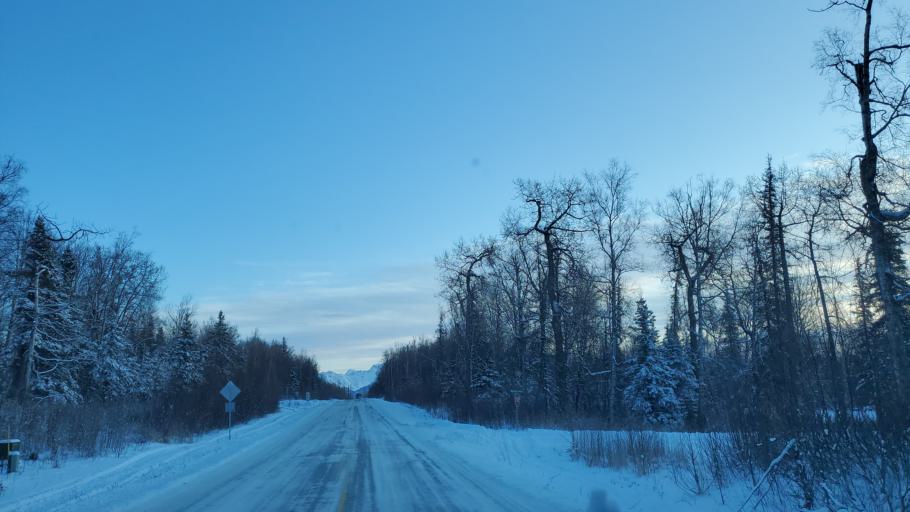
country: US
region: Alaska
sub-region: Matanuska-Susitna Borough
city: Lakes
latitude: 61.6356
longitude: -149.3032
